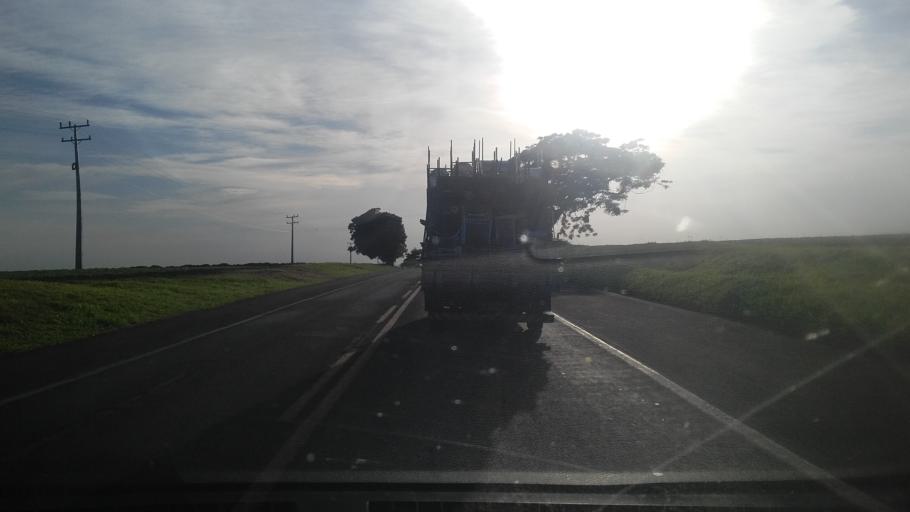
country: BR
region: Parana
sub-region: Bandeirantes
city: Bandeirantes
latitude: -23.1461
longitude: -50.5671
